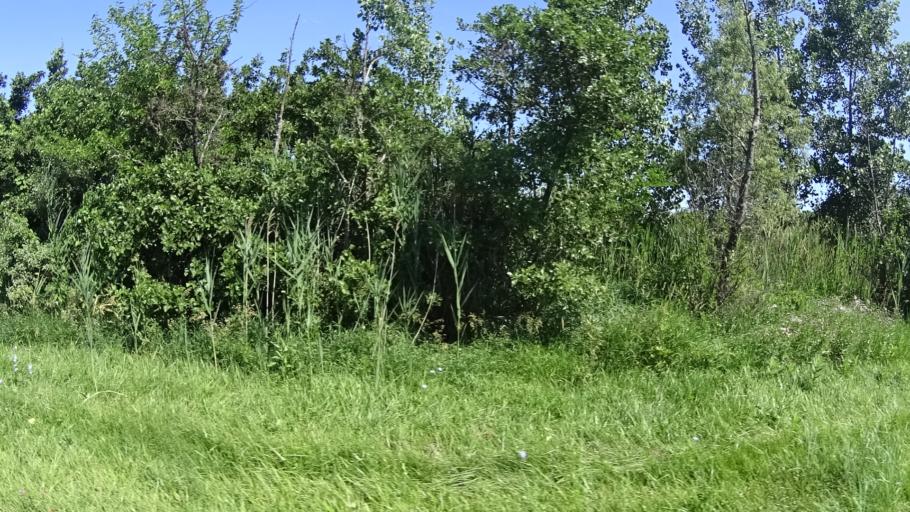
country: US
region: Ohio
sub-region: Ottawa County
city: Port Clinton
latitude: 41.4356
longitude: -82.8654
